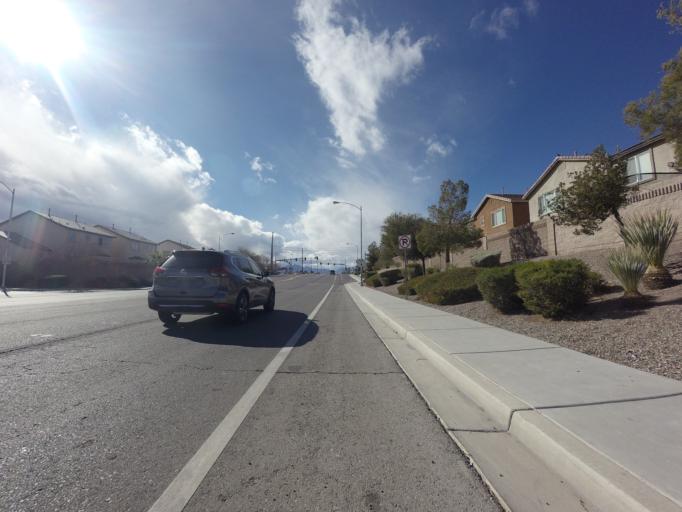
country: US
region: Nevada
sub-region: Clark County
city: North Las Vegas
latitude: 36.2543
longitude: -115.1333
